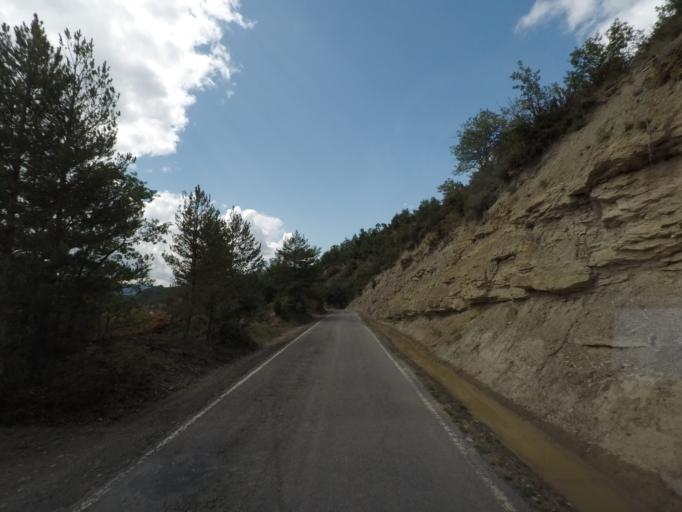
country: ES
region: Aragon
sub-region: Provincia de Huesca
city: Yebra de Basa
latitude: 42.4011
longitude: -0.2535
